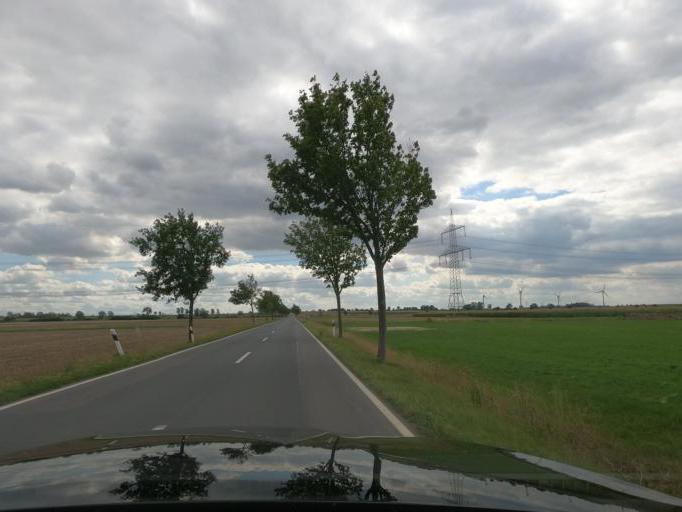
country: DE
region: Lower Saxony
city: Hohenhameln
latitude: 52.3029
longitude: 10.0444
